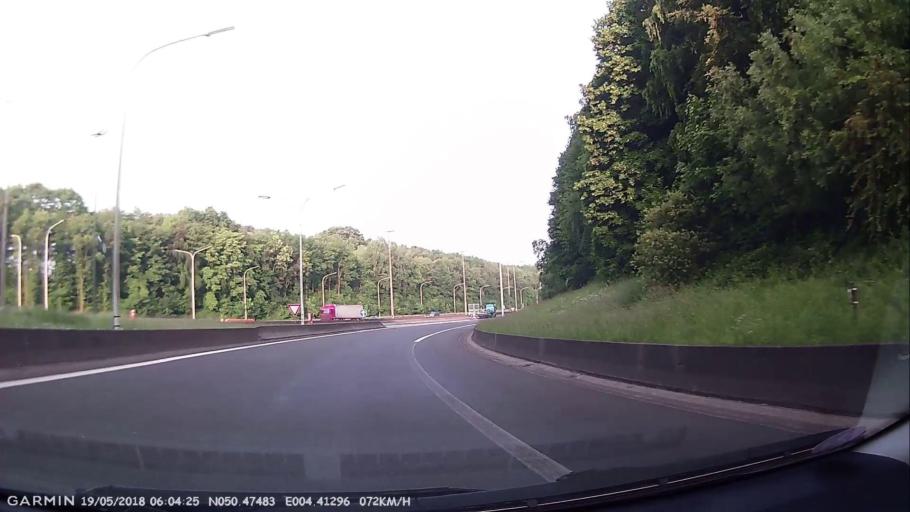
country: BE
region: Wallonia
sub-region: Province du Hainaut
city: Brunehault
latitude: 50.4746
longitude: 4.4126
